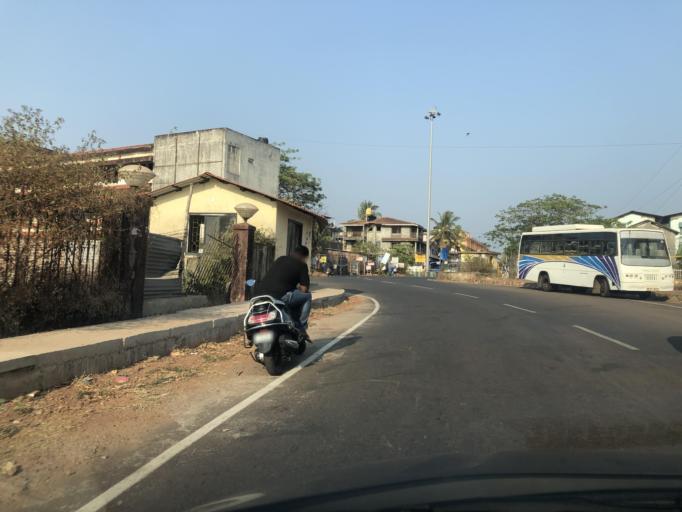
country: IN
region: Goa
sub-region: North Goa
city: Serula
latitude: 15.5260
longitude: 73.8293
